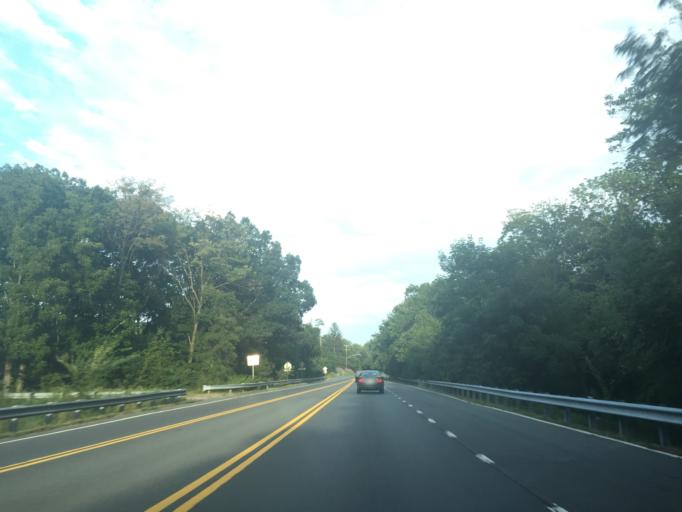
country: US
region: Maryland
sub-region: Montgomery County
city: Spencerville
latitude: 39.1181
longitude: -76.9752
